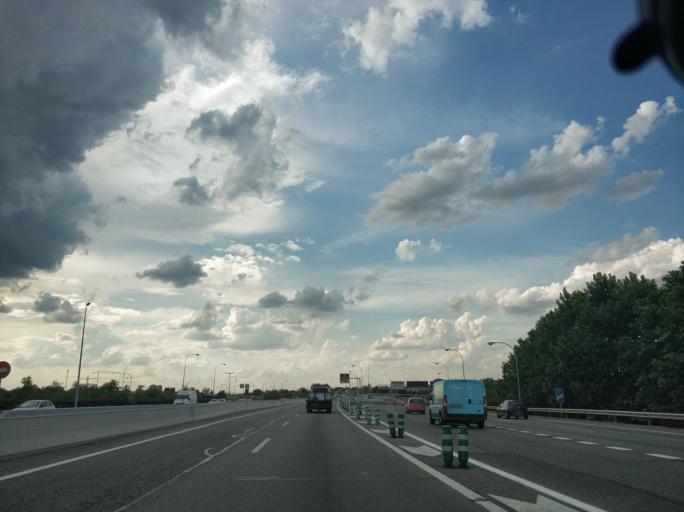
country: ES
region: Madrid
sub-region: Provincia de Madrid
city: Usera
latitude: 40.3776
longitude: -3.6846
